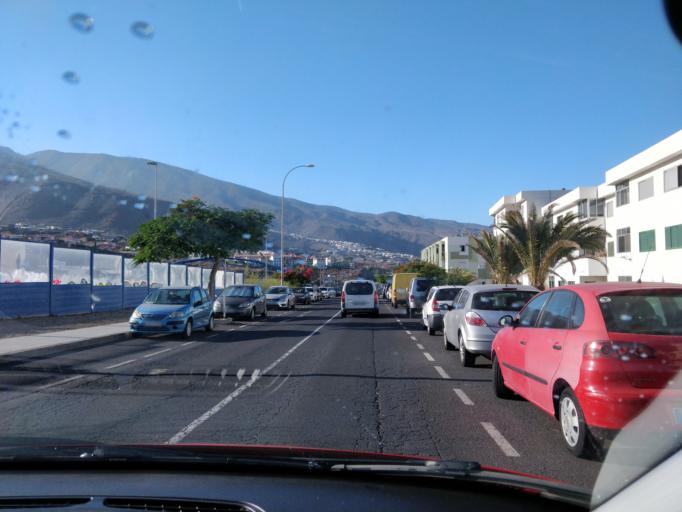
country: ES
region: Canary Islands
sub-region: Provincia de Santa Cruz de Tenerife
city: Candelaria
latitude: 28.3527
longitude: -16.3730
